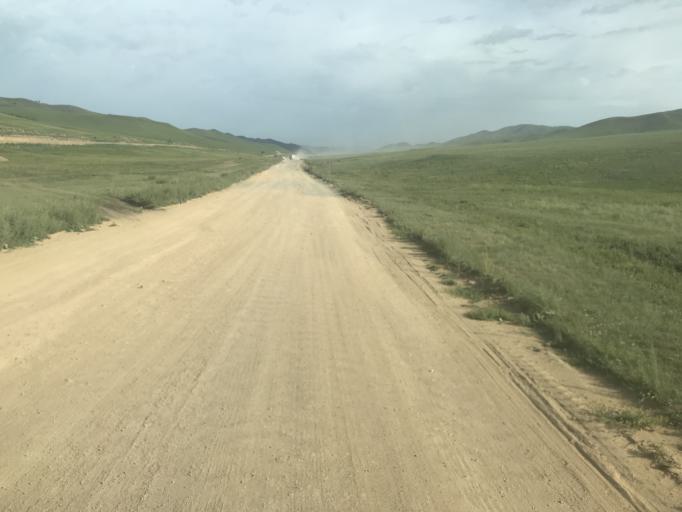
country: MN
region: Central Aimak
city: Javhlant
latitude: 48.7378
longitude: 106.1306
